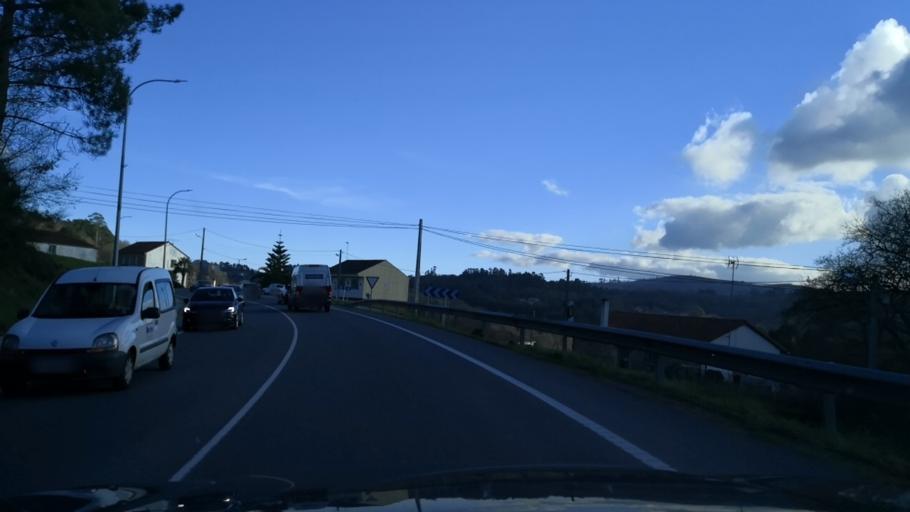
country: ES
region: Galicia
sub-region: Provincia de Pontevedra
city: Silleda
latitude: 42.7025
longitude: -8.2586
